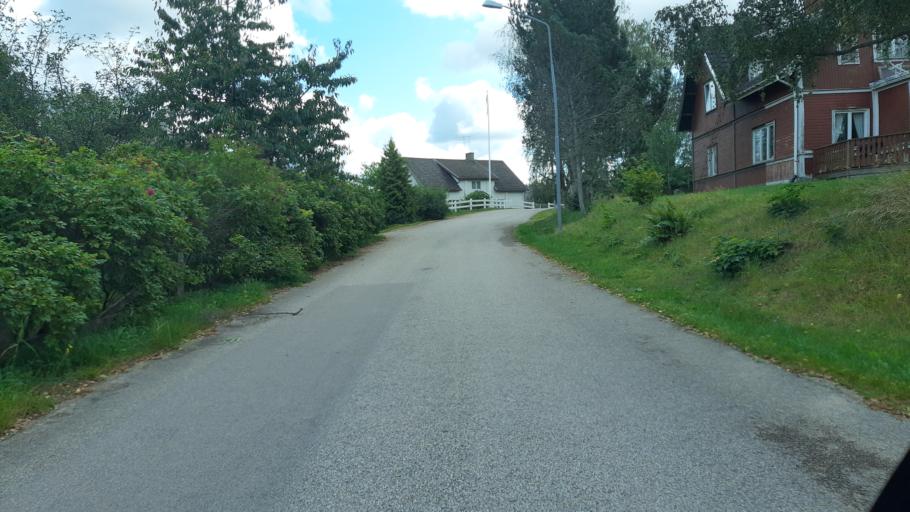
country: SE
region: Kronoberg
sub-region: Tingsryds Kommun
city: Tingsryd
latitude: 56.5058
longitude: 15.1517
